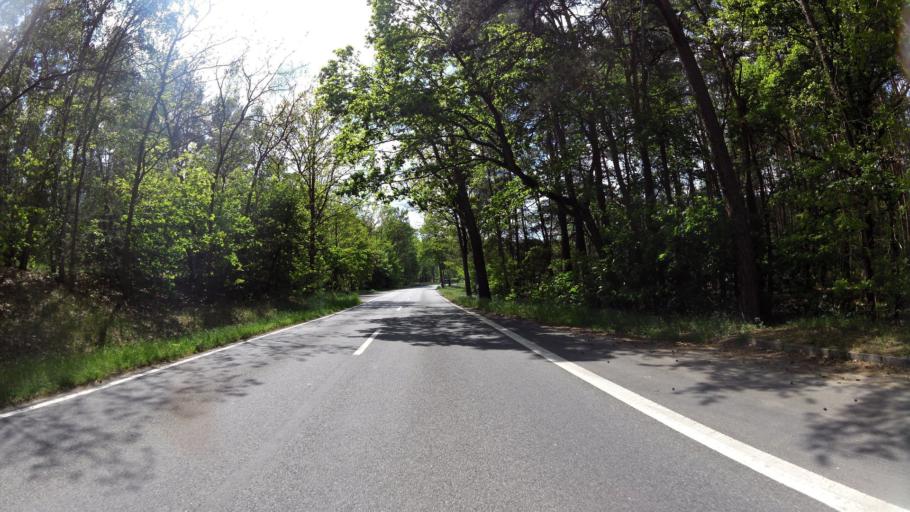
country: DE
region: Brandenburg
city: Gross Koris
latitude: 52.1616
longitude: 13.6716
